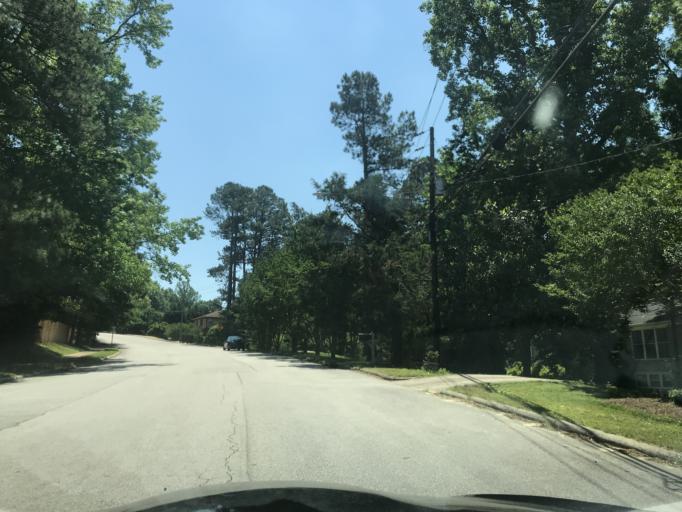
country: US
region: North Carolina
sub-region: Wake County
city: West Raleigh
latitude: 35.8538
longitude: -78.6601
